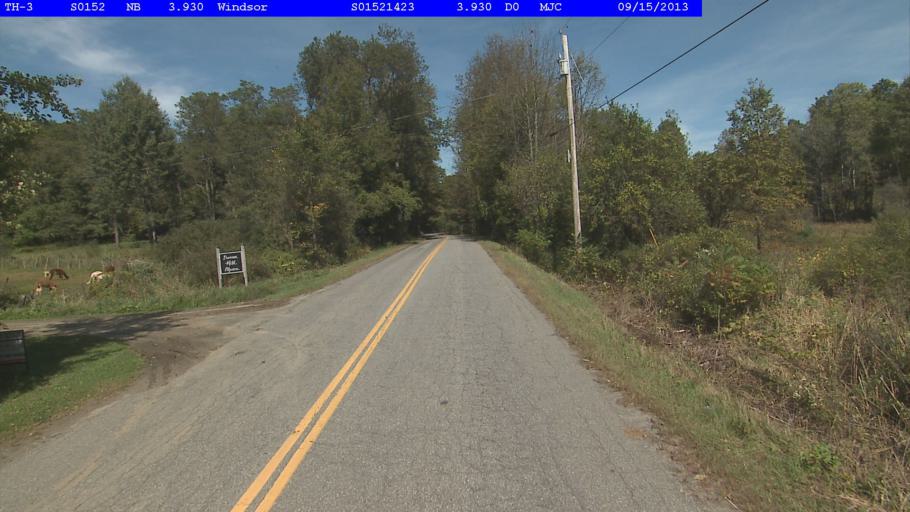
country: US
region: Vermont
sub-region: Windsor County
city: Windsor
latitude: 43.5172
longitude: -72.4333
